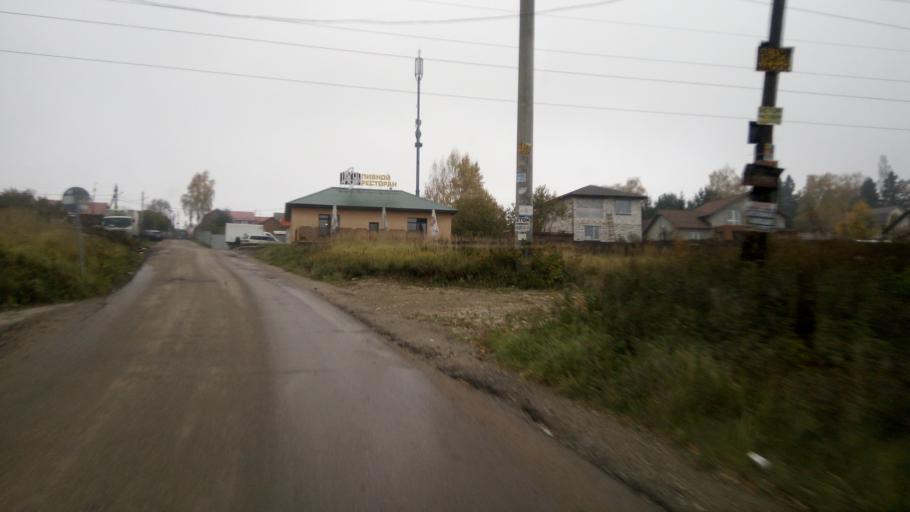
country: RU
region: Moskovskaya
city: Skhodnya
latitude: 55.9355
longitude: 37.2878
